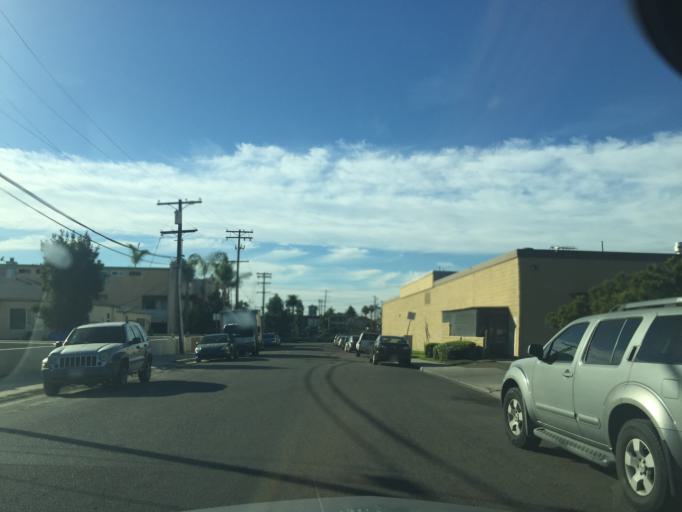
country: US
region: California
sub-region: San Diego County
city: San Diego
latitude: 32.7543
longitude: -117.1227
